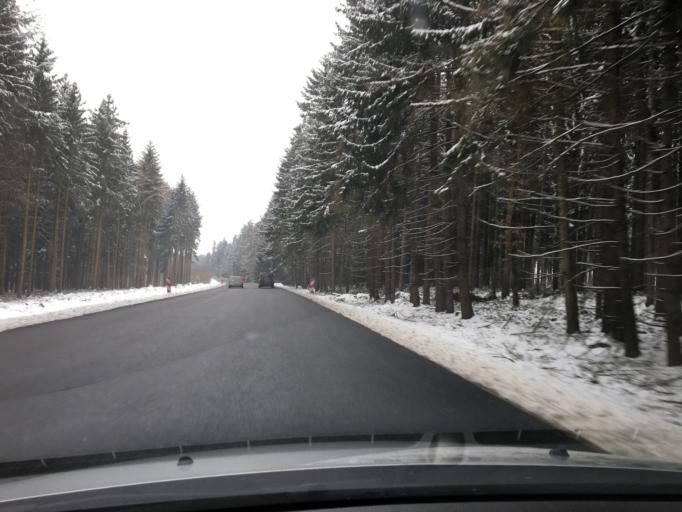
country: DE
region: Bavaria
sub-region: Upper Bavaria
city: Egglkofen
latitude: 48.4102
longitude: 12.4377
